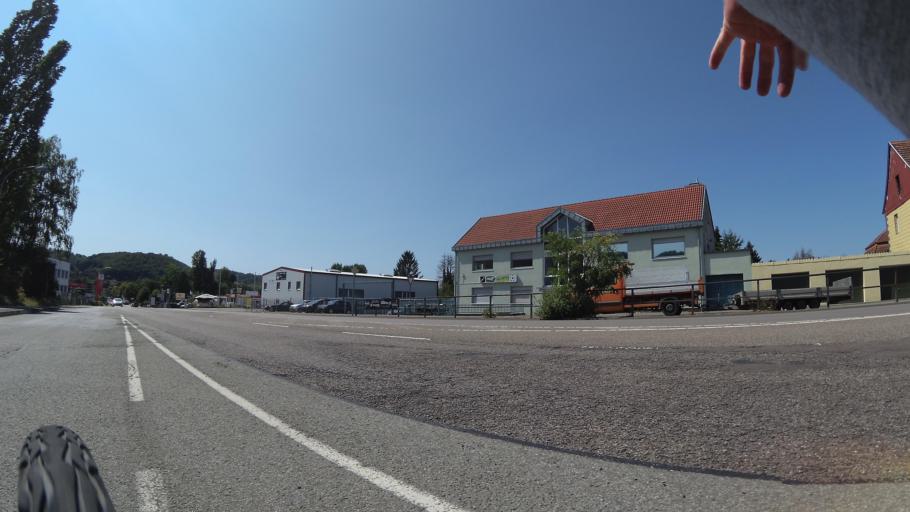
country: FR
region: Lorraine
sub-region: Departement de la Moselle
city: Spicheren
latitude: 49.2109
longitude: 6.9646
